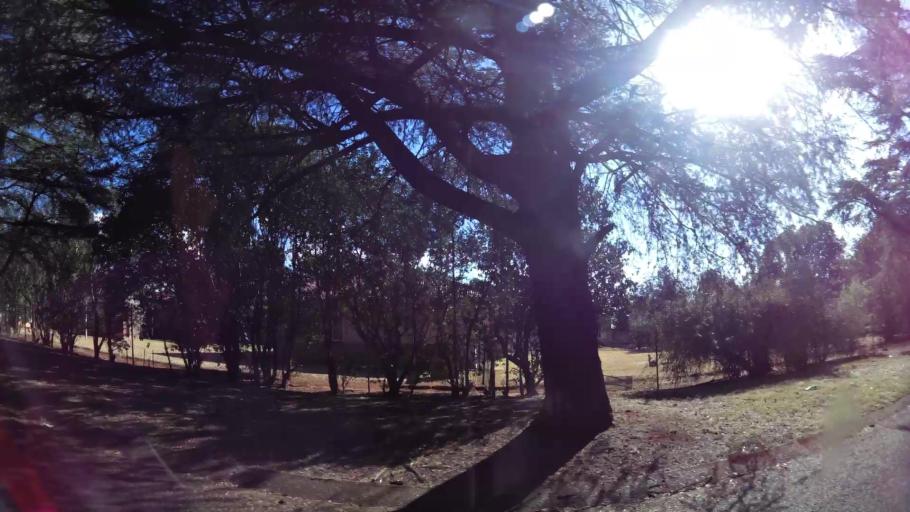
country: ZA
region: Gauteng
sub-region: West Rand District Municipality
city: Carletonville
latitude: -26.3728
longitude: 27.4042
